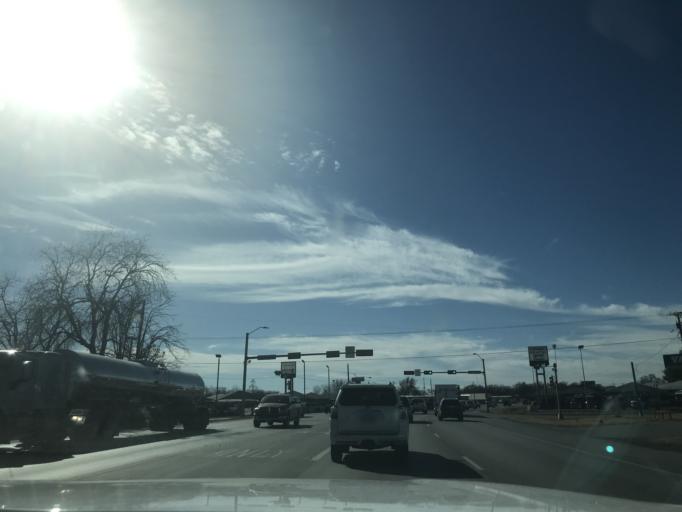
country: US
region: Texas
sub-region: Erath County
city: Stephenville
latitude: 32.2051
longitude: -98.2098
